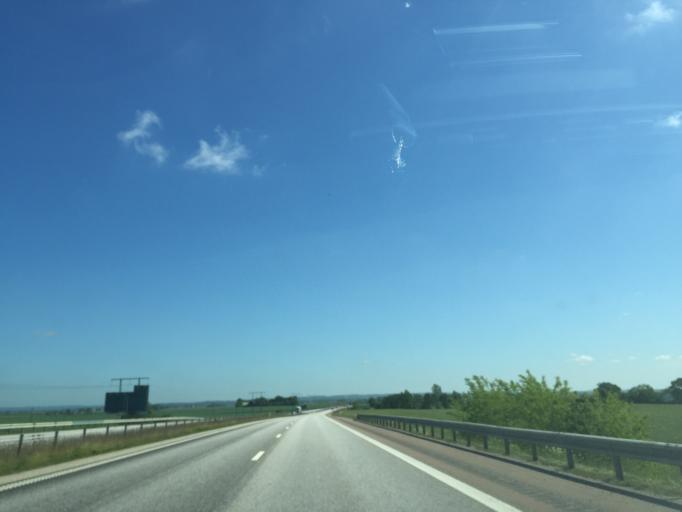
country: SE
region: Skane
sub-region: Astorps Kommun
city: Astorp
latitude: 56.1515
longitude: 12.9447
